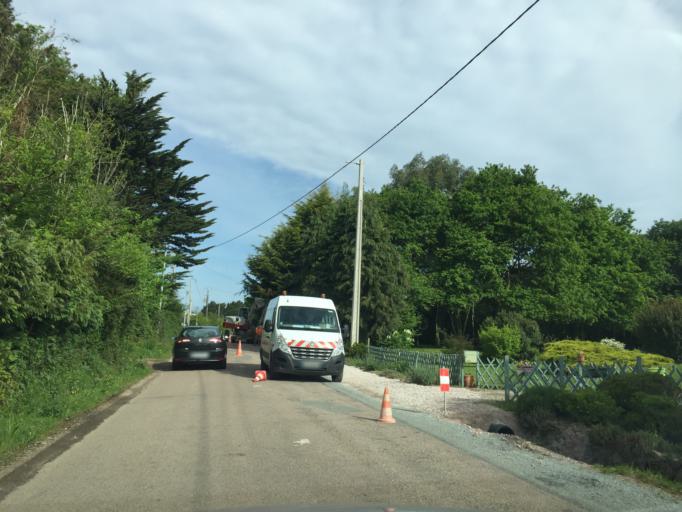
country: FR
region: Brittany
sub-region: Departement des Cotes-d'Armor
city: Matignon
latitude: 48.6480
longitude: -2.3268
